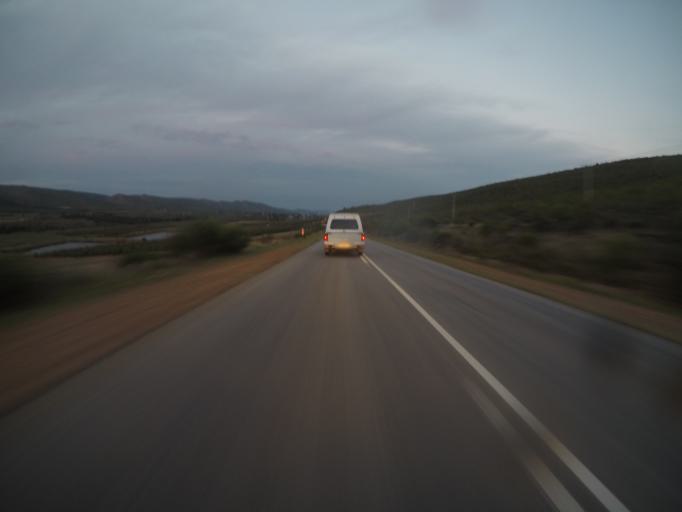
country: ZA
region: Western Cape
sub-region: Eden District Municipality
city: Plettenberg Bay
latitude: -33.8101
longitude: 23.7071
